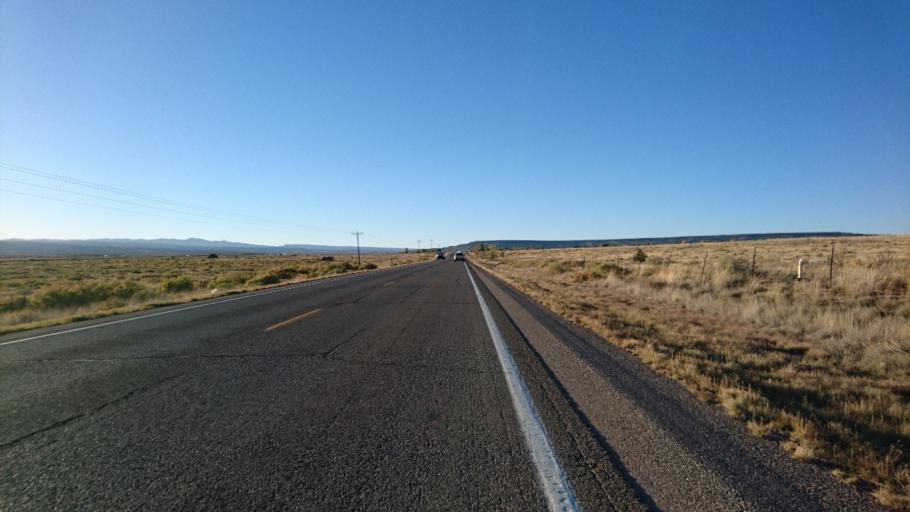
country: US
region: New Mexico
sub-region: Cibola County
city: Grants
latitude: 35.1214
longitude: -107.7958
